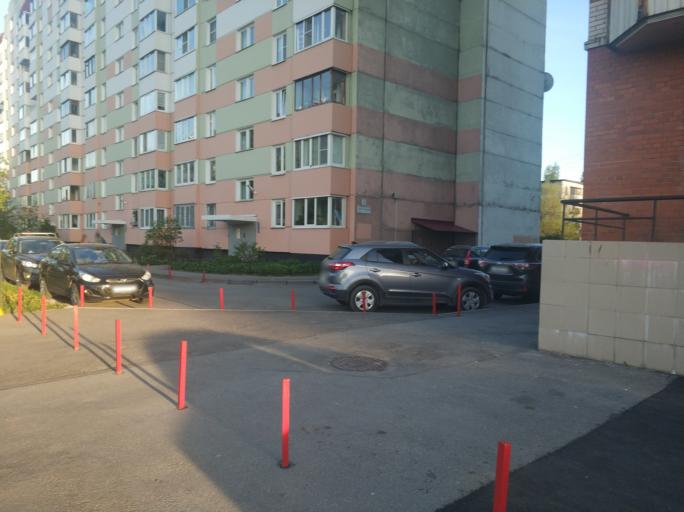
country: RU
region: St.-Petersburg
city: Grazhdanka
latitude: 60.0354
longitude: 30.3867
